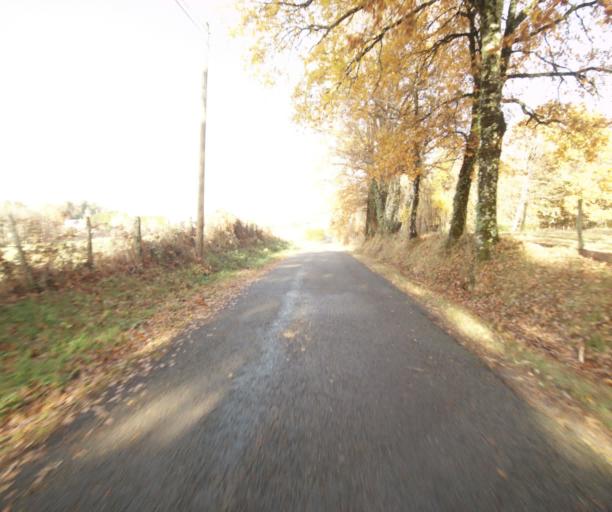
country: FR
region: Limousin
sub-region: Departement de la Correze
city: Cornil
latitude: 45.2061
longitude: 1.7093
